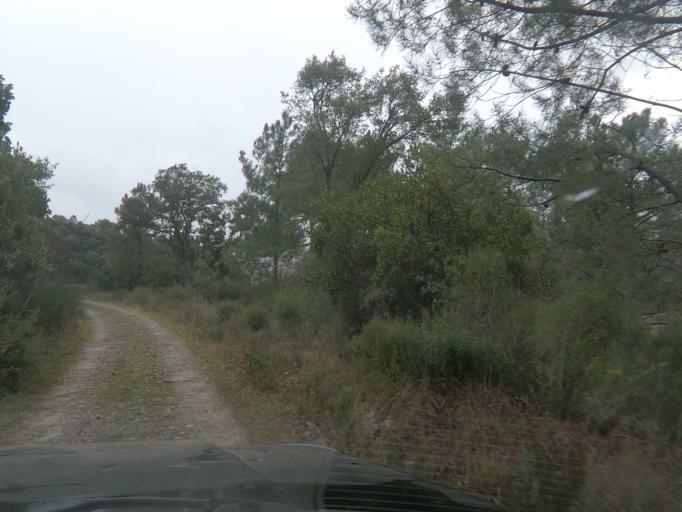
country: PT
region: Vila Real
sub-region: Vila Real
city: Vila Real
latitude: 41.2545
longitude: -7.7449
